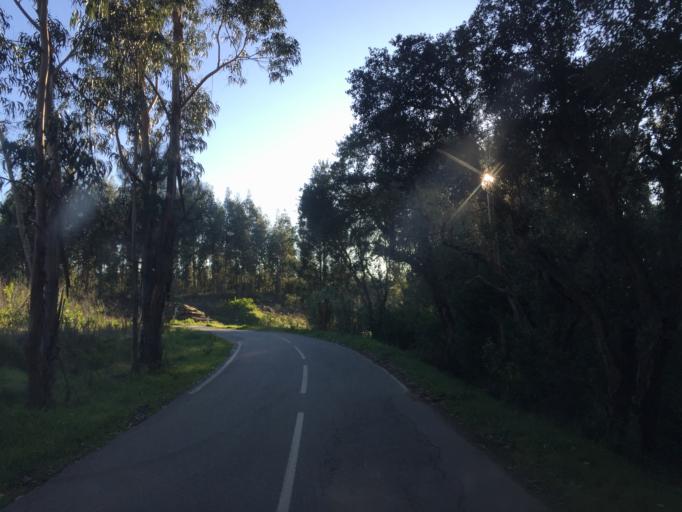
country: PT
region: Coimbra
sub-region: Figueira da Foz
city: Alhadas
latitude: 40.1597
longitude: -8.8007
